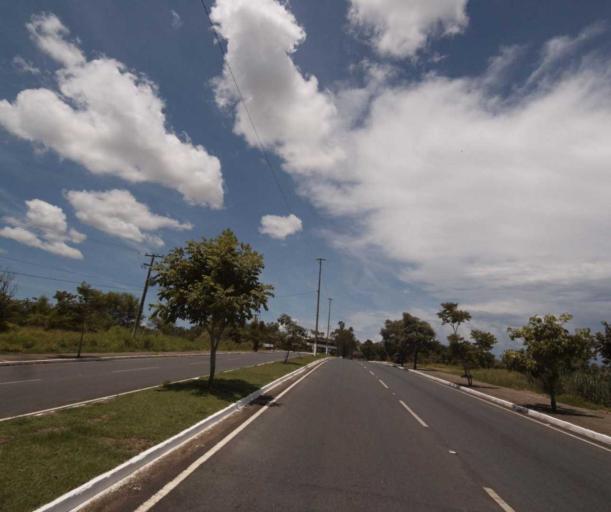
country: BR
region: Mato Grosso
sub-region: Cuiaba
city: Cuiaba
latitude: -15.5696
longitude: -56.1071
